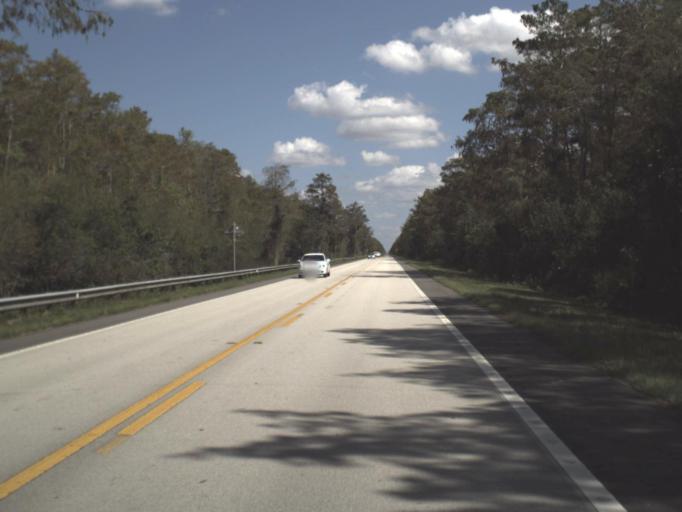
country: US
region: Florida
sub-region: Miami-Dade County
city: Kendall West
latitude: 25.8553
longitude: -81.0183
